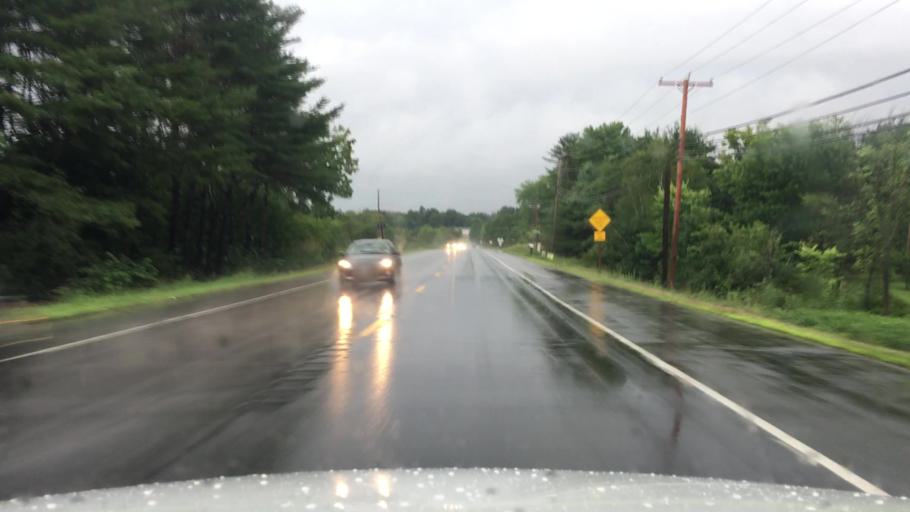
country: US
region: Maine
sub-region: Kennebec County
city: Manchester
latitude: 44.3216
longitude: -69.8991
